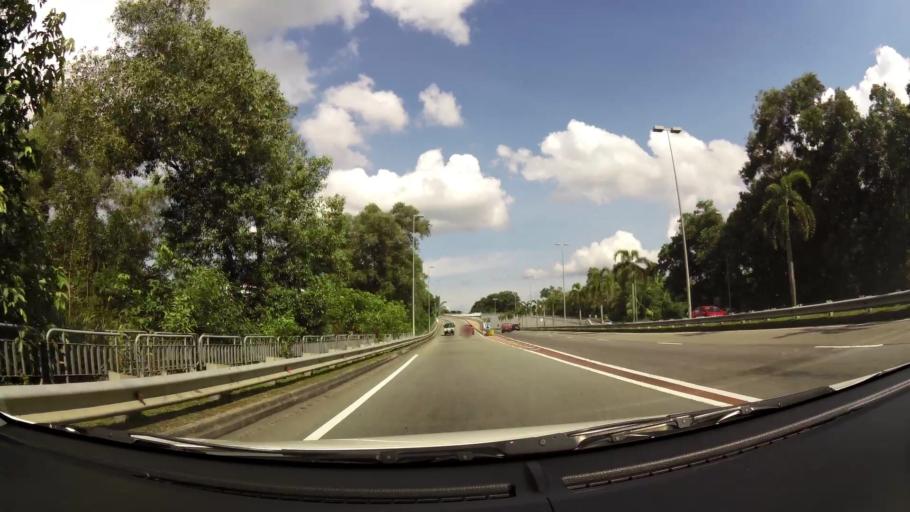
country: BN
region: Brunei and Muara
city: Bandar Seri Begawan
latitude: 4.9516
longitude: 114.9613
